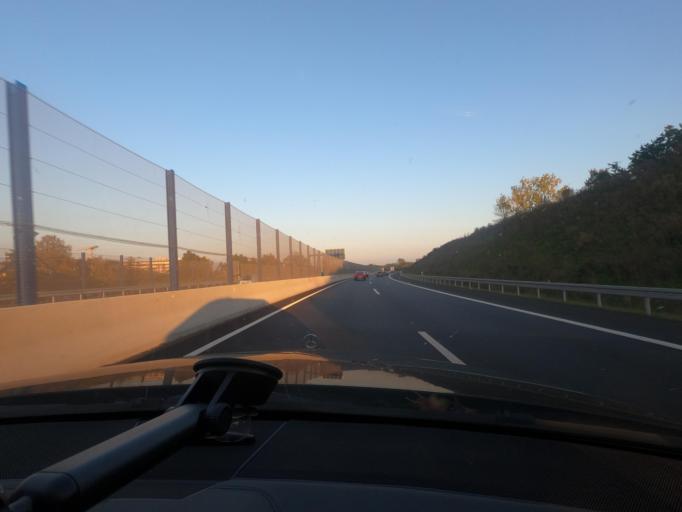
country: DE
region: North Rhine-Westphalia
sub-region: Regierungsbezirk Arnsberg
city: Bochum
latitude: 51.4629
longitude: 7.2534
